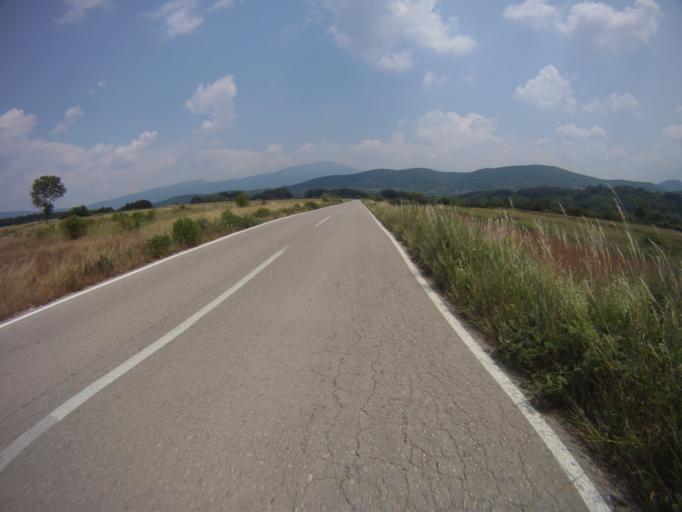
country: RS
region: Central Serbia
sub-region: Nisavski Okrug
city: Gadzin Han
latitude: 43.2067
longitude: 22.0094
